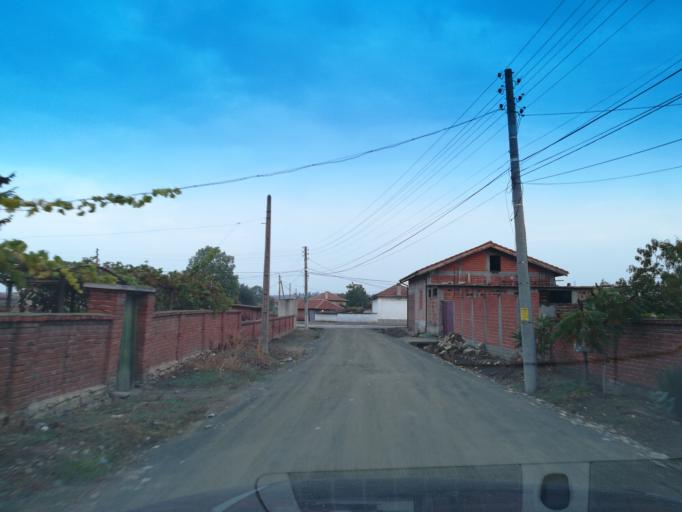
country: BG
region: Stara Zagora
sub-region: Obshtina Chirpan
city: Chirpan
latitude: 42.1721
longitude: 25.2089
